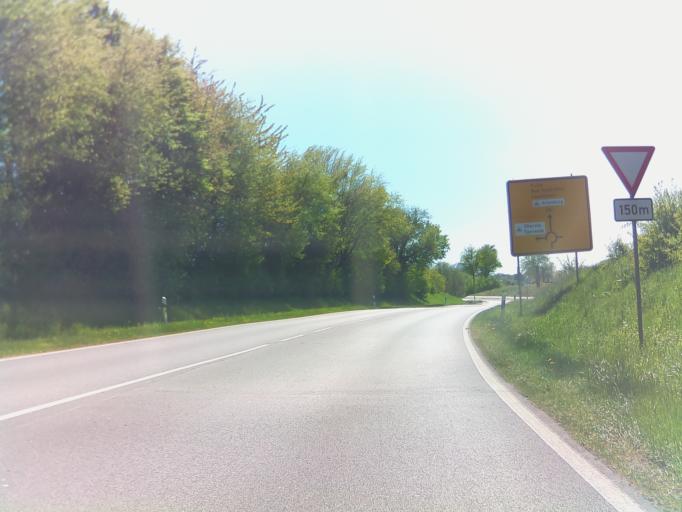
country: DE
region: Hesse
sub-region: Regierungsbezirk Giessen
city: Alsfeld
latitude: 50.7418
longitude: 9.2851
